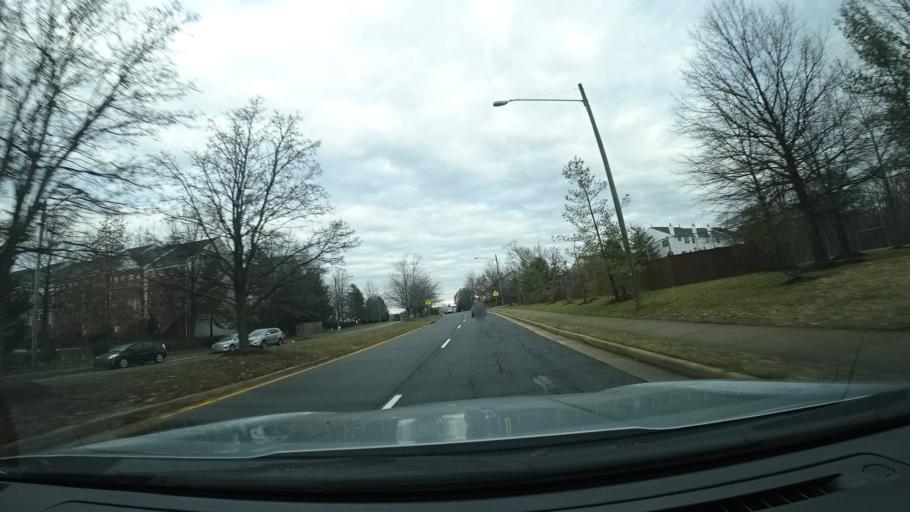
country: US
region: Virginia
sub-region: Fairfax County
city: Floris
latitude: 38.9432
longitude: -77.4057
